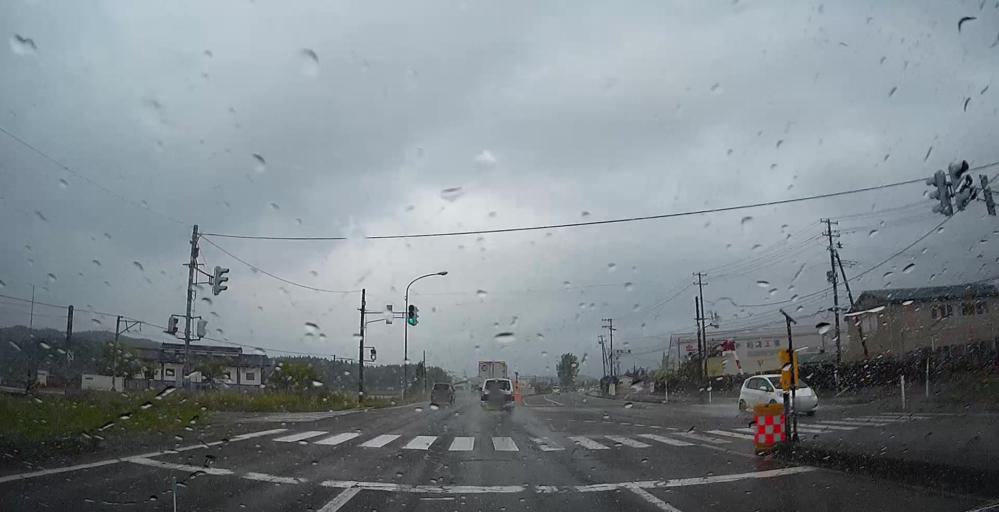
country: JP
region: Niigata
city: Kashiwazaki
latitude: 37.4438
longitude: 138.6336
